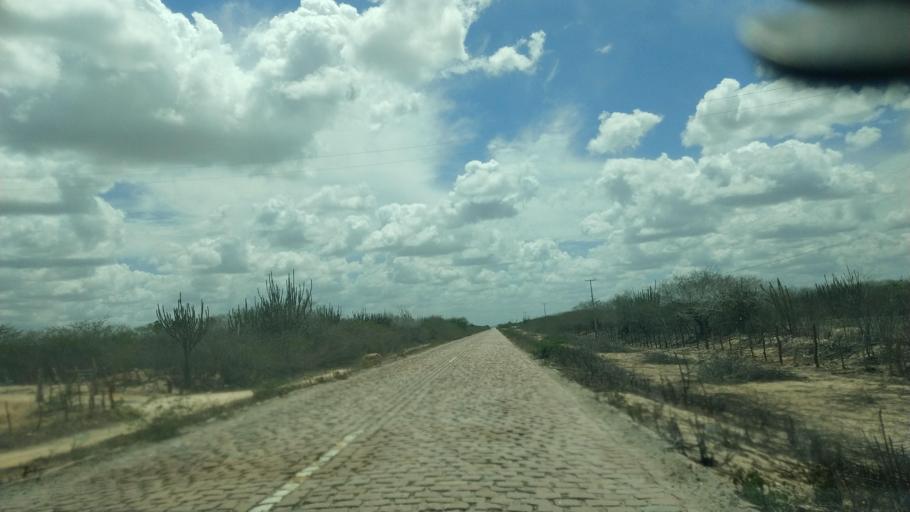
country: BR
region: Rio Grande do Norte
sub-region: Sao Paulo Do Potengi
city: Sao Paulo do Potengi
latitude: -5.9655
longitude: -35.8513
